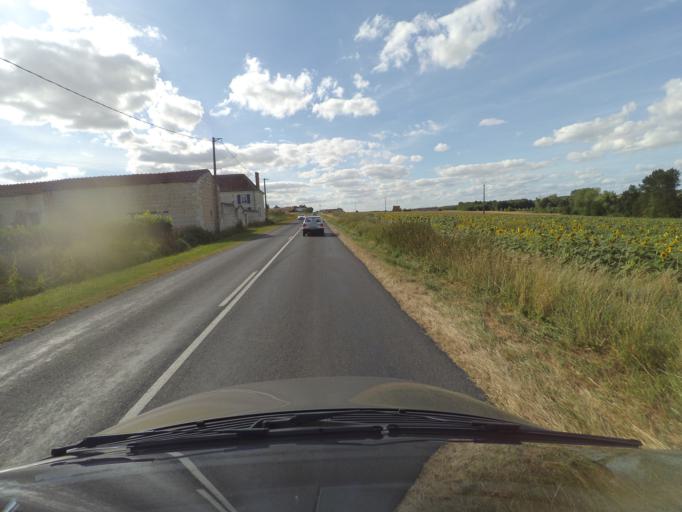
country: FR
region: Poitou-Charentes
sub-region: Departement de la Vienne
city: Saint-Gervais-les-Trois-Clochers
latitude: 46.9535
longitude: 0.4044
